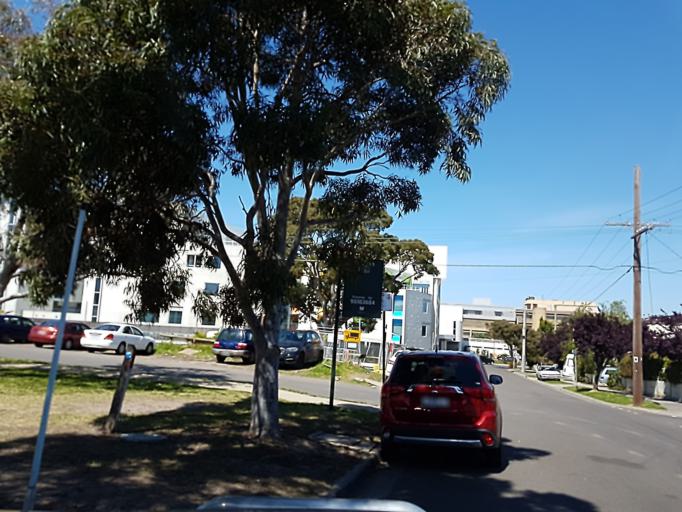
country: AU
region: Victoria
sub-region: Monash
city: Clayton
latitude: -37.9183
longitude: 145.1236
